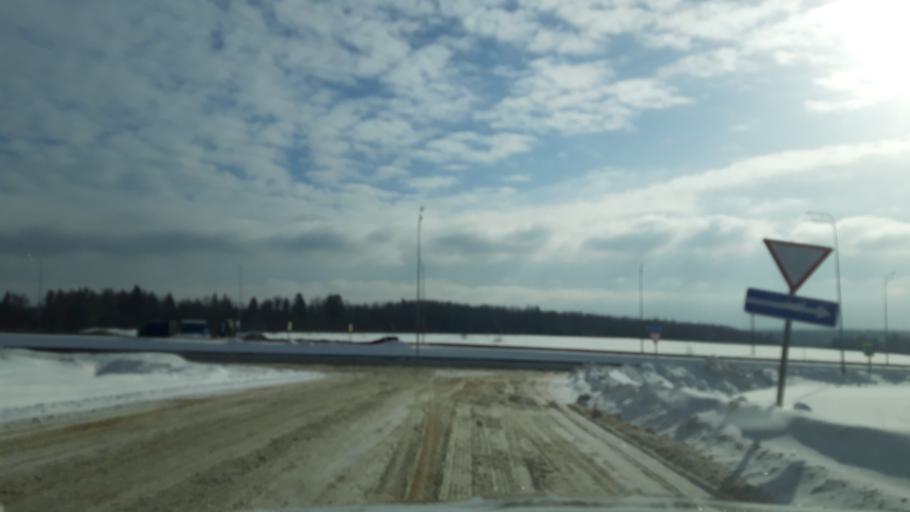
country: RU
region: Moskovskaya
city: Yermolino
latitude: 56.1354
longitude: 37.3776
